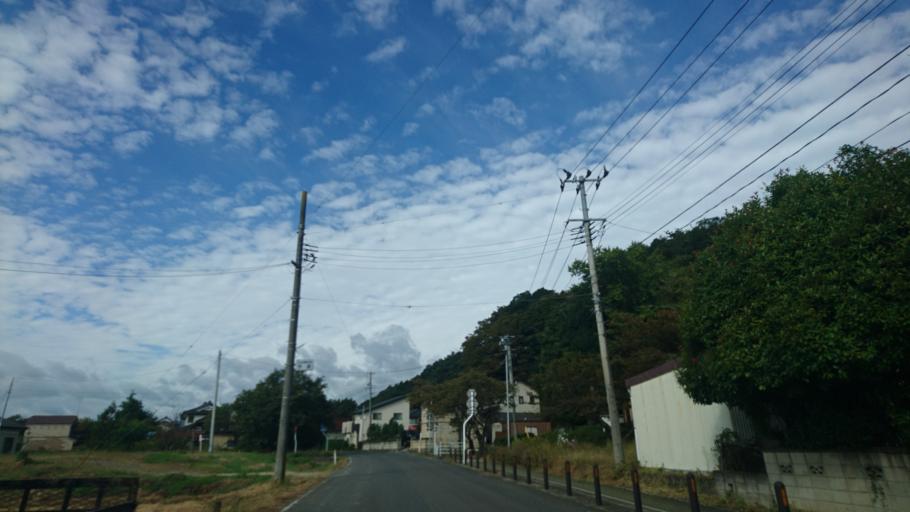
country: JP
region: Fukushima
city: Sukagawa
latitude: 37.3284
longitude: 140.2756
